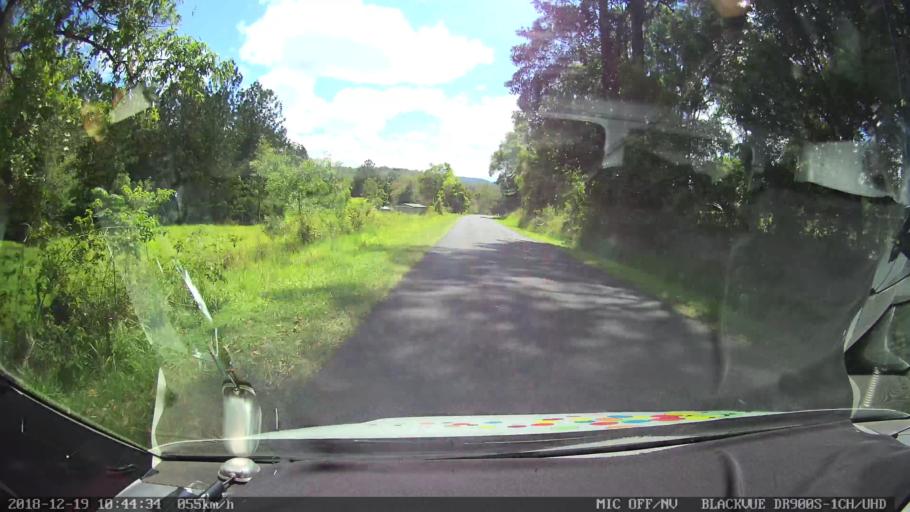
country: AU
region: New South Wales
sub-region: Lismore Municipality
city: Nimbin
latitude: -28.5955
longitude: 153.1819
